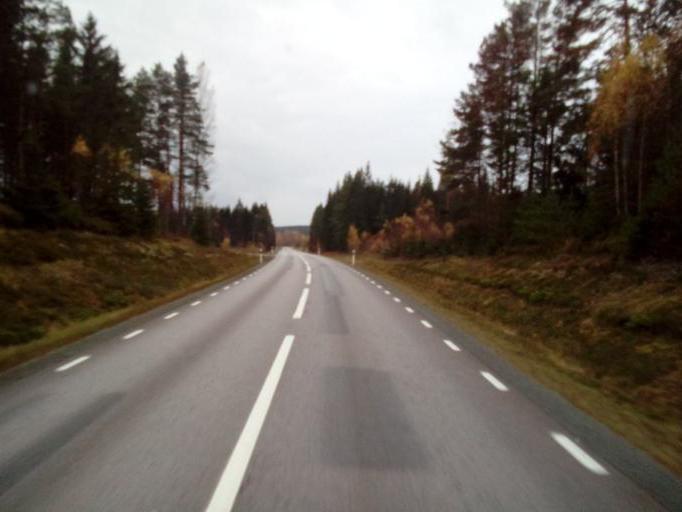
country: SE
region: OErebro
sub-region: Laxa Kommun
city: Laxa
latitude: 59.0806
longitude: 14.5337
